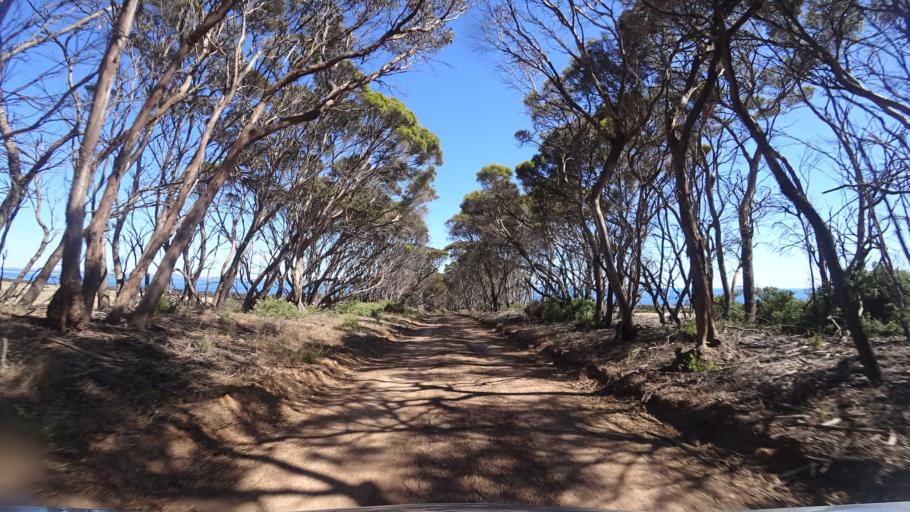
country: AU
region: South Australia
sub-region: Kangaroo Island
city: Kingscote
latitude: -35.7434
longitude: 137.7220
